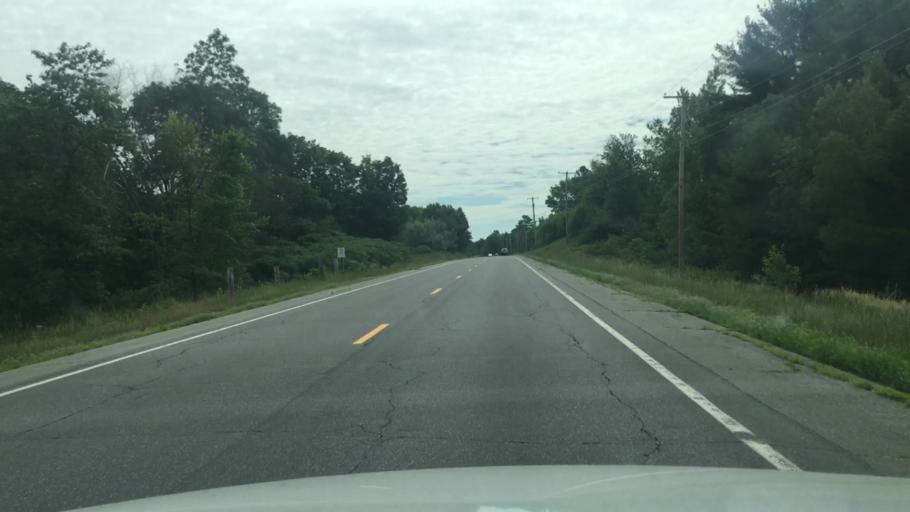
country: US
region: Maine
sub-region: Waldo County
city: Burnham
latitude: 44.6155
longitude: -69.3785
